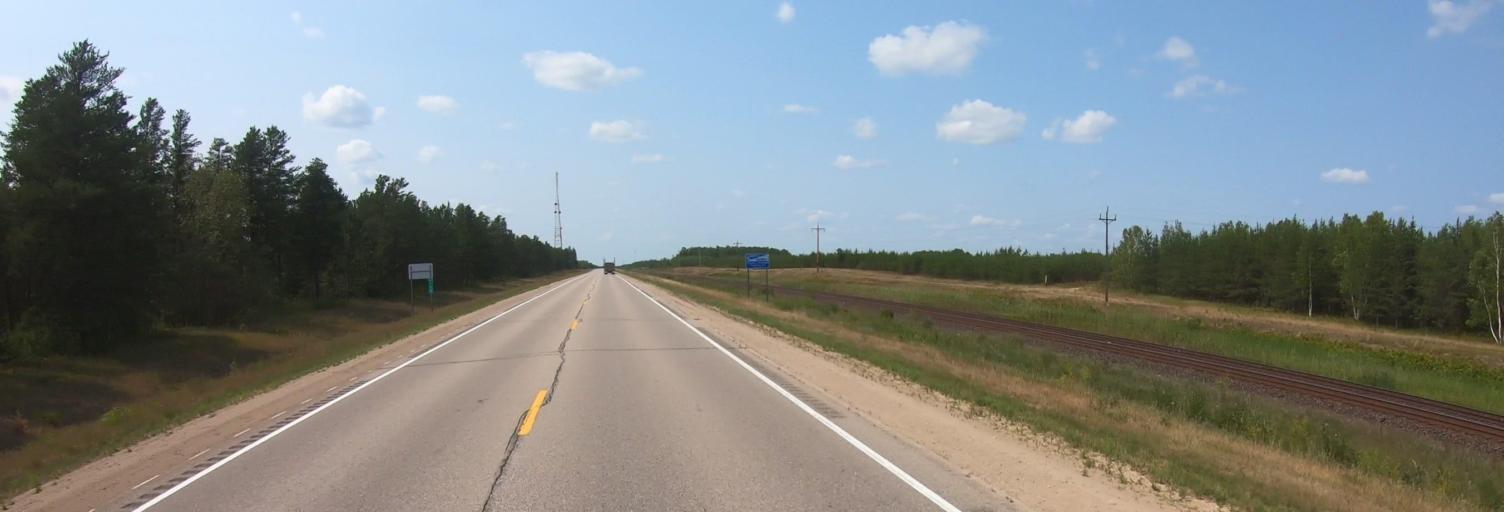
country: US
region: Minnesota
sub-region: Roseau County
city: Warroad
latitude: 48.7872
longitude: -95.0405
